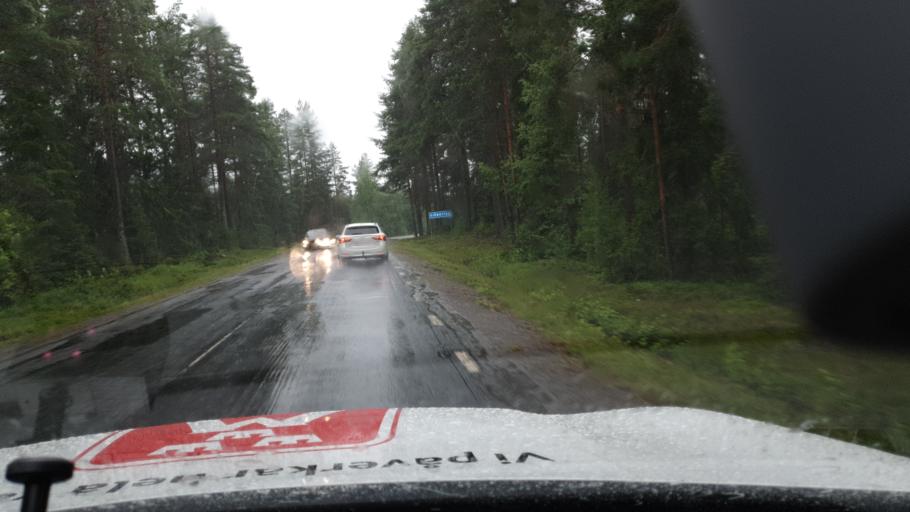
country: SE
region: Vaesterbotten
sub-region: Skelleftea Kommun
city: Burea
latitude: 64.6026
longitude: 21.0945
